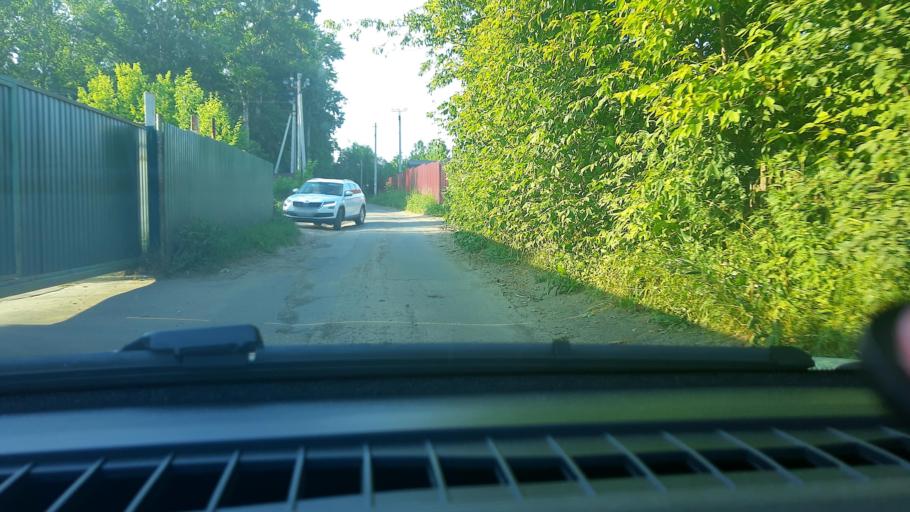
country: RU
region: Nizjnij Novgorod
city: Nizhniy Novgorod
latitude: 56.1908
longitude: 43.9432
